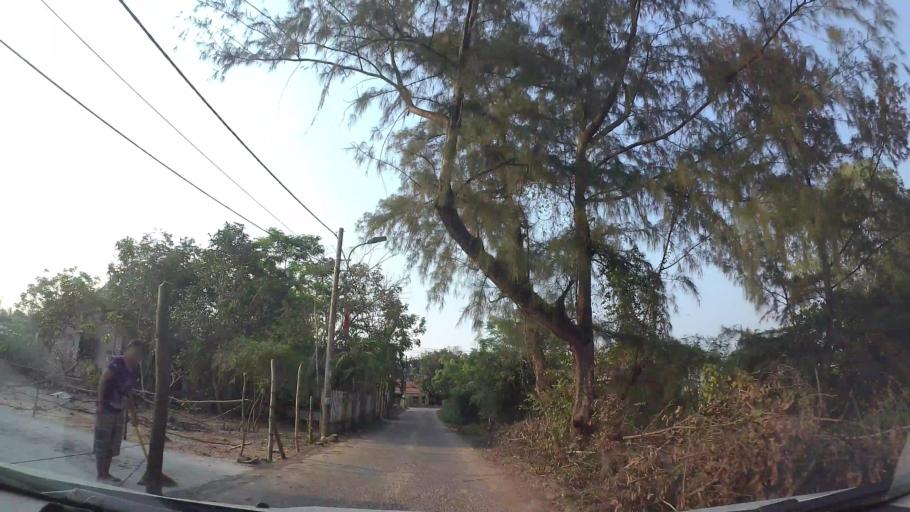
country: VN
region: Da Nang
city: Ngu Hanh Son
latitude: 15.9726
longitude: 108.2436
